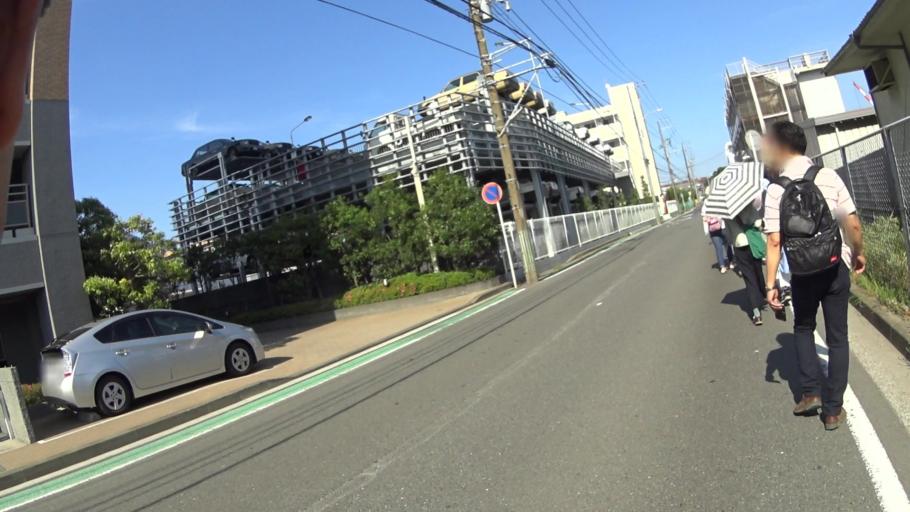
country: JP
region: Kanagawa
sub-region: Kawasaki-shi
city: Kawasaki
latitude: 35.4957
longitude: 139.6858
